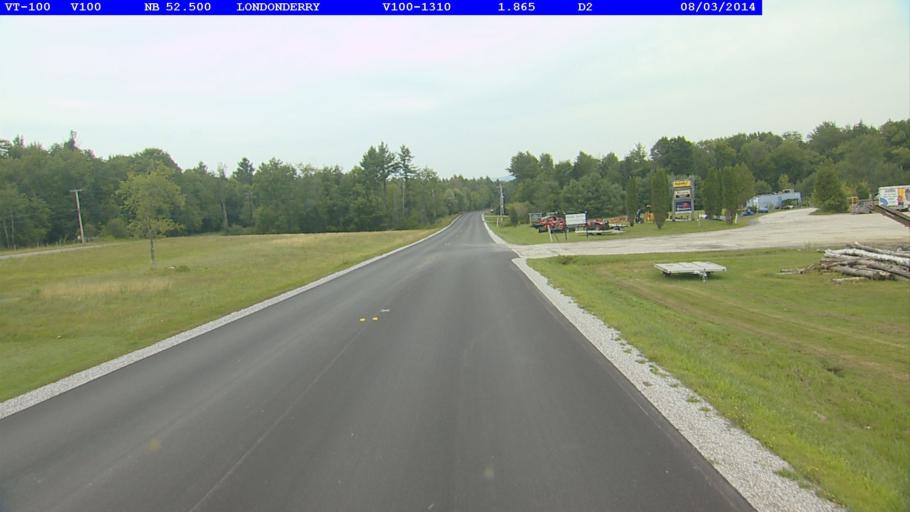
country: US
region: Vermont
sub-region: Windham County
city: Dover
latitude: 43.1780
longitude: -72.8195
